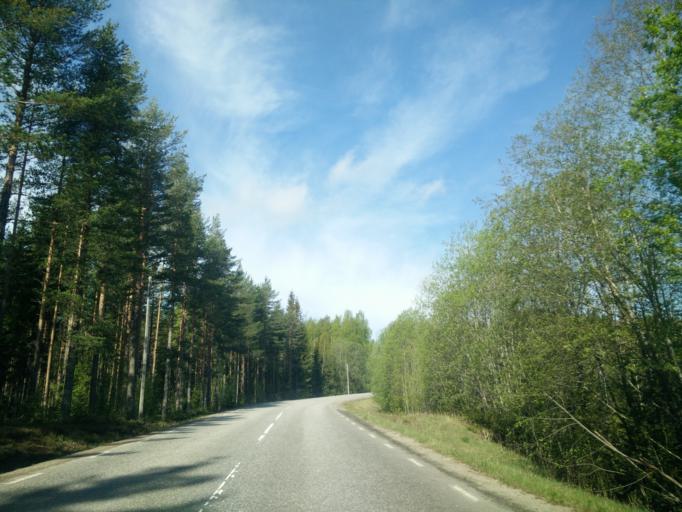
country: SE
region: Vaesternorrland
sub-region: Sundsvalls Kommun
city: Nolby
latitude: 62.2996
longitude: 17.3205
